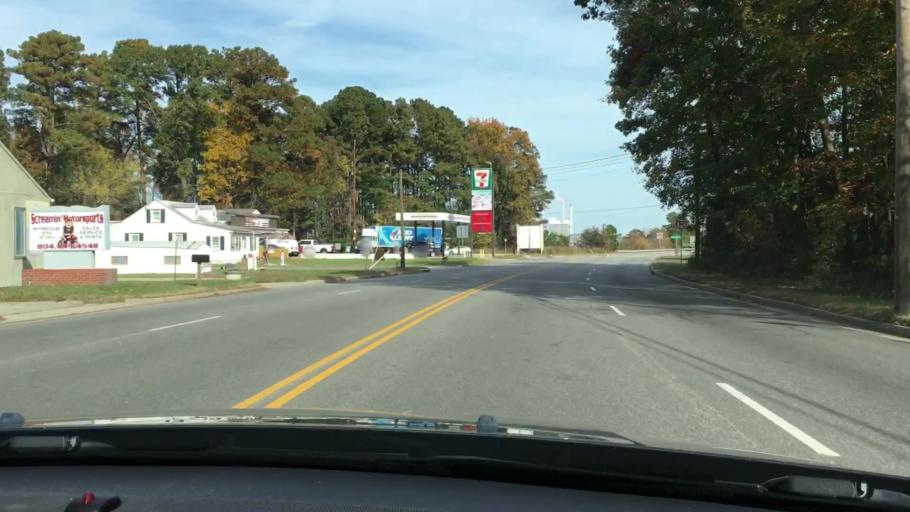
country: US
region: Virginia
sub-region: King William County
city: West Point
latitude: 37.5285
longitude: -76.8208
